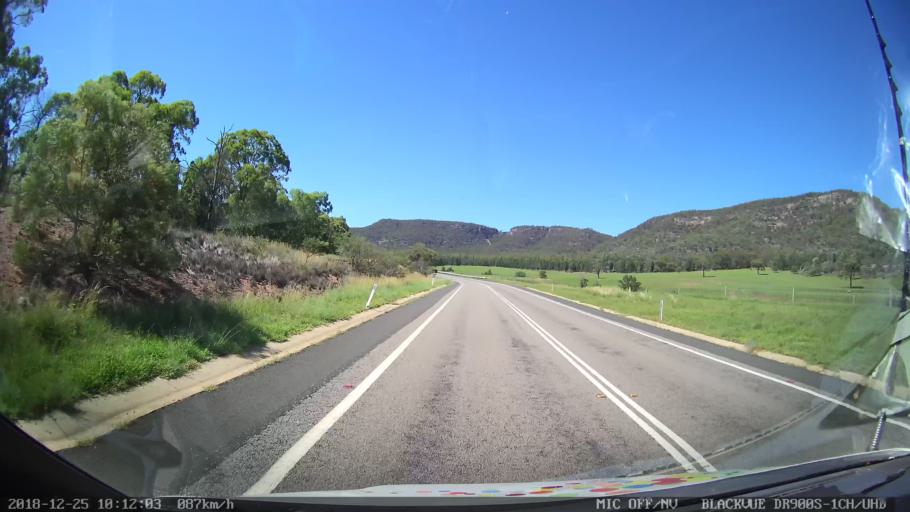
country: AU
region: New South Wales
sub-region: Muswellbrook
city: Denman
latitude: -32.3244
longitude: 150.5289
